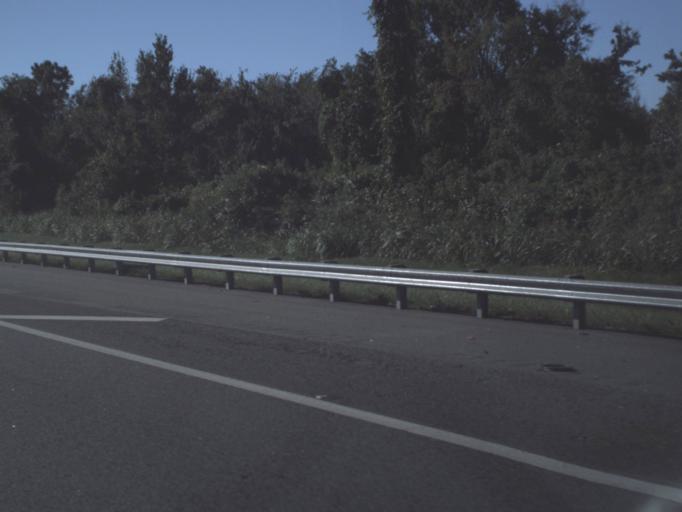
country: US
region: Florida
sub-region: Seminole County
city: Sanford
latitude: 28.7657
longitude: -81.2725
